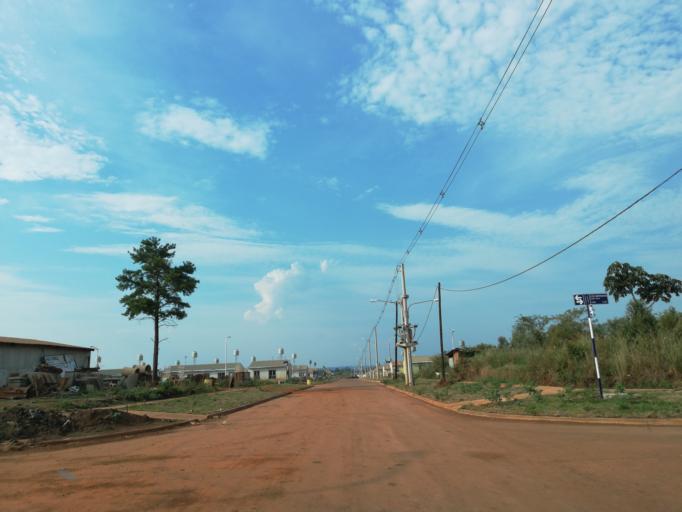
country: AR
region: Misiones
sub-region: Departamento de Capital
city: Posadas
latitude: -27.4019
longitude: -55.9911
